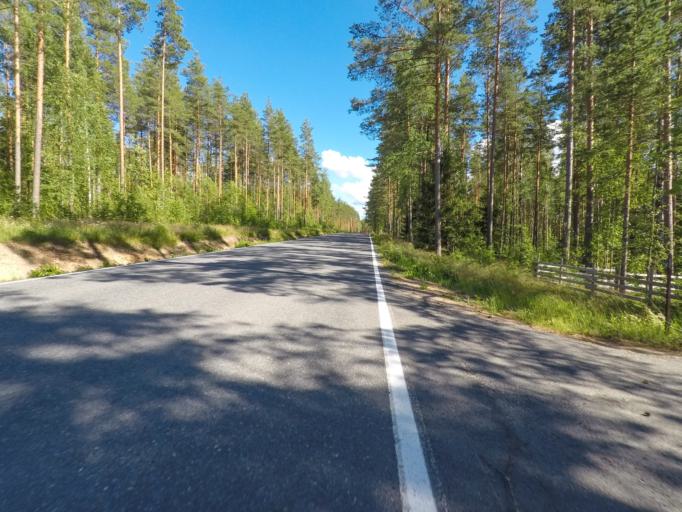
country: FI
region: South Karelia
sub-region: Lappeenranta
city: Taipalsaari
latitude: 61.1779
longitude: 28.0098
